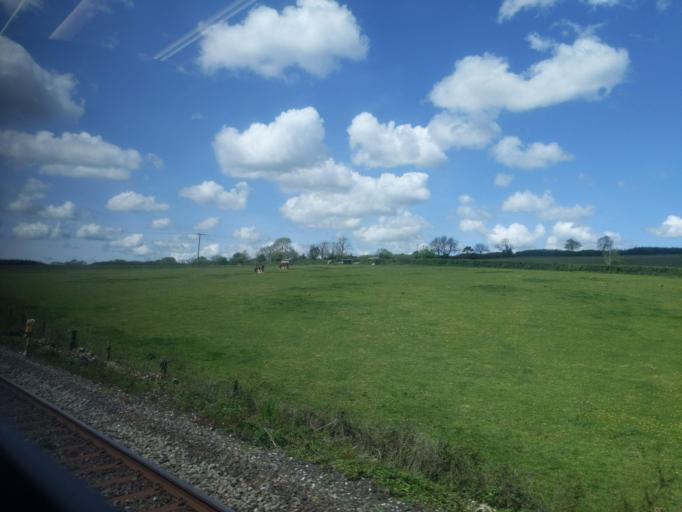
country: GB
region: England
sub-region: Cornwall
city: Pillaton
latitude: 50.4195
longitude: -4.3773
